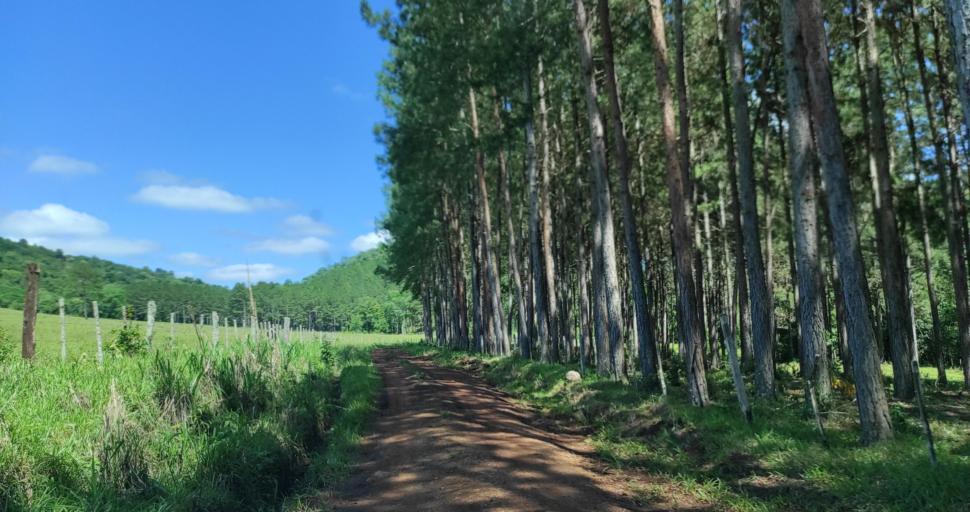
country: AR
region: Misiones
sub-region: Departamento de Veinticinco de Mayo
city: Veinticinco de Mayo
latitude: -27.4196
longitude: -54.7090
